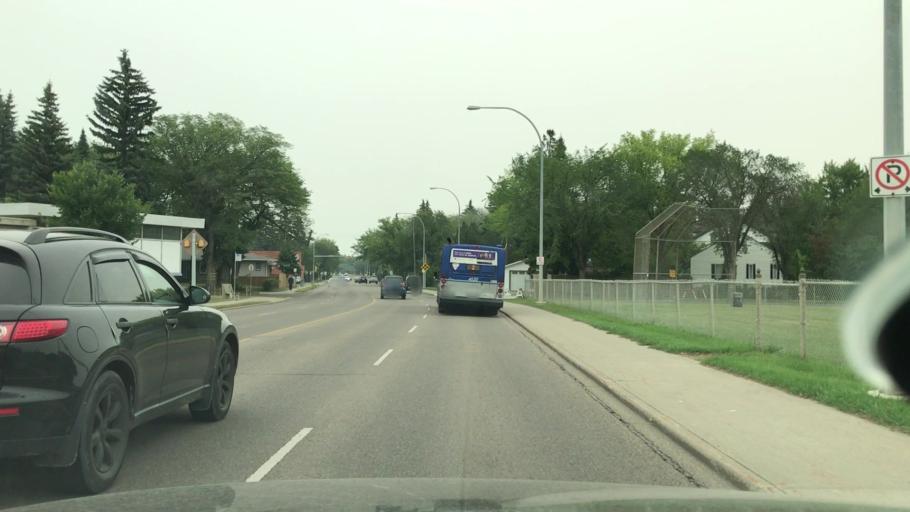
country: CA
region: Alberta
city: Edmonton
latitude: 53.5448
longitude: -113.5557
